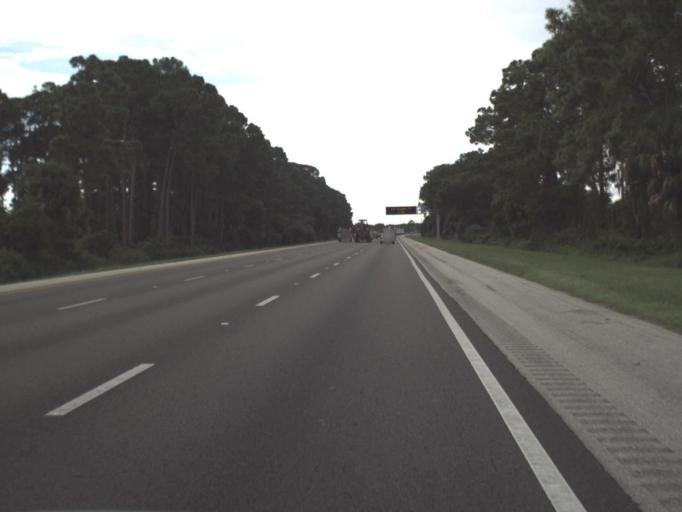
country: US
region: Florida
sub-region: Sarasota County
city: Osprey
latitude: 27.2173
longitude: -82.4476
